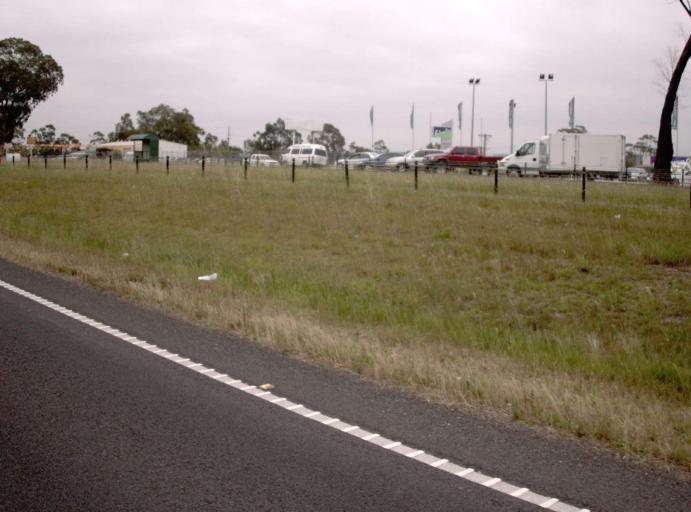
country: AU
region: Victoria
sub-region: Latrobe
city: Traralgon
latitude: -38.2089
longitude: 146.4960
